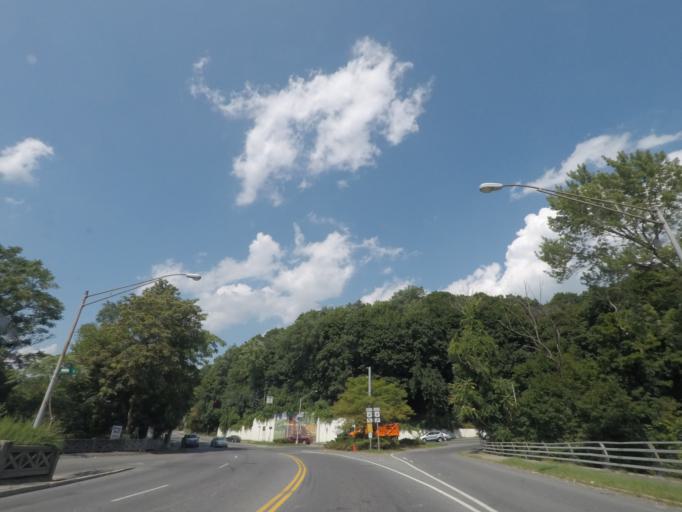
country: US
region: New York
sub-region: Rensselaer County
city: Troy
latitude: 42.7040
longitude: -73.6964
